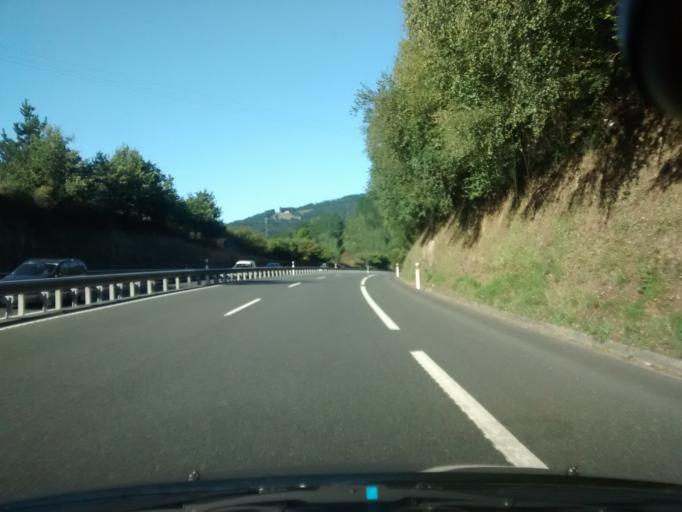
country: ES
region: Basque Country
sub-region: Provincia de Guipuzcoa
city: Elgoibar
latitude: 43.2169
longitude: -2.4075
